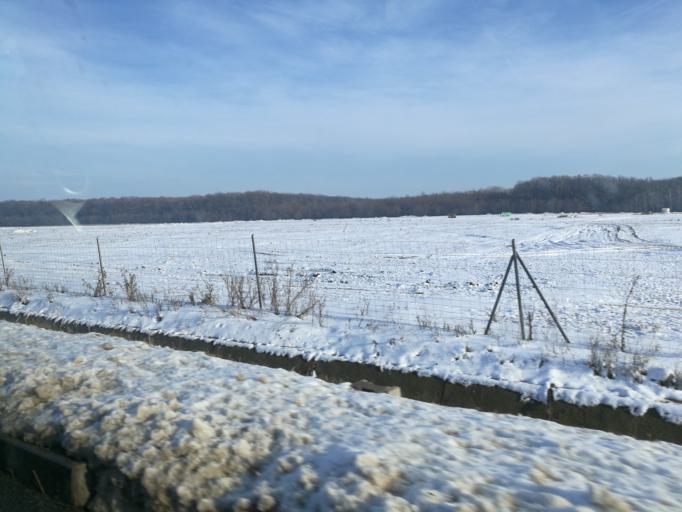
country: RO
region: Ilfov
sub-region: Voluntari City
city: Voluntari
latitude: 44.5105
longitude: 26.1646
